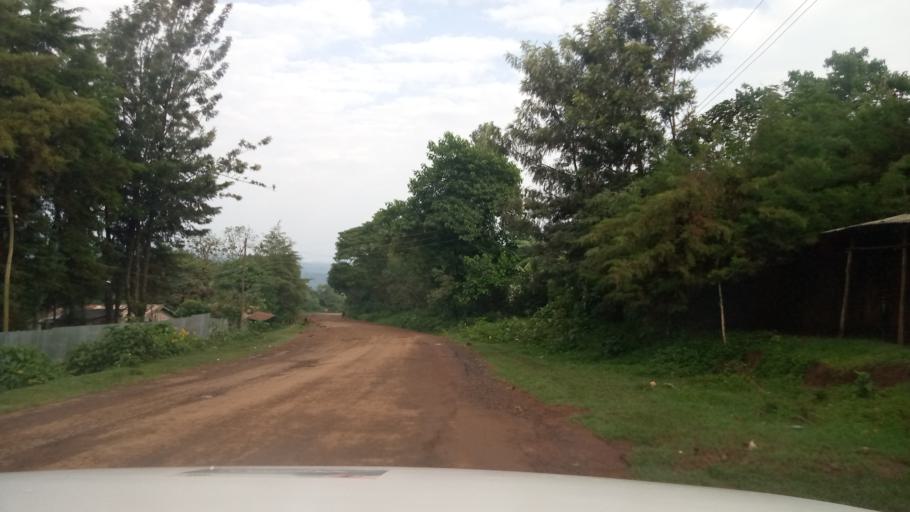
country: ET
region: Oromiya
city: Agaro
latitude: 7.7974
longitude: 36.7202
